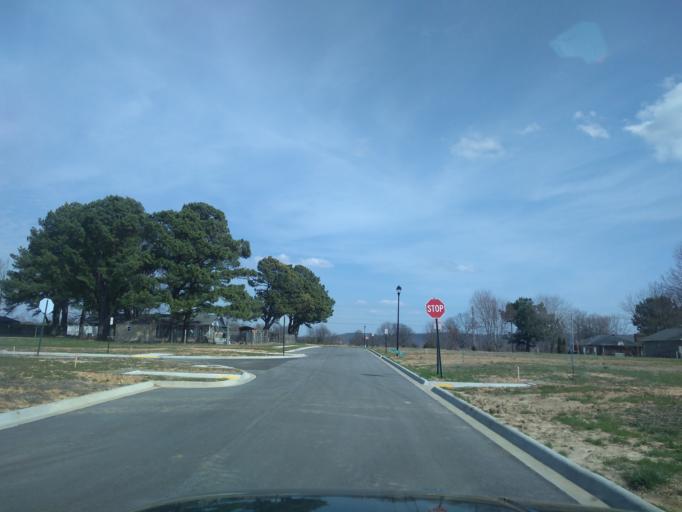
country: US
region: Arkansas
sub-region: Washington County
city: Farmington
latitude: 36.0698
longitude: -94.2415
